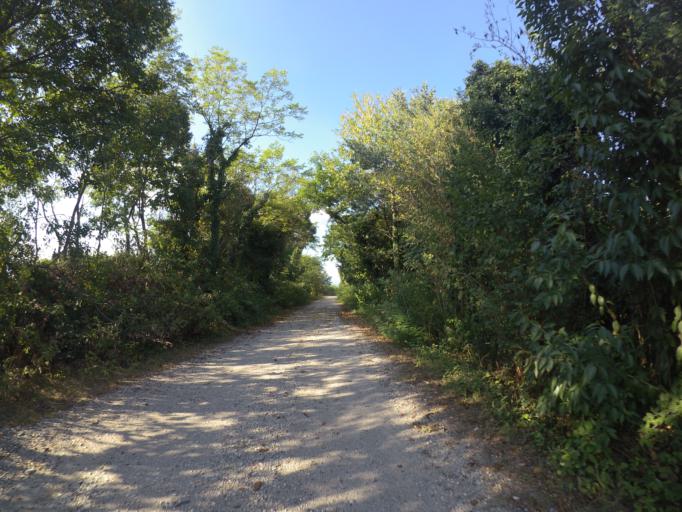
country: IT
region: Friuli Venezia Giulia
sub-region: Provincia di Udine
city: Basaldella
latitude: 46.0193
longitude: 13.1946
